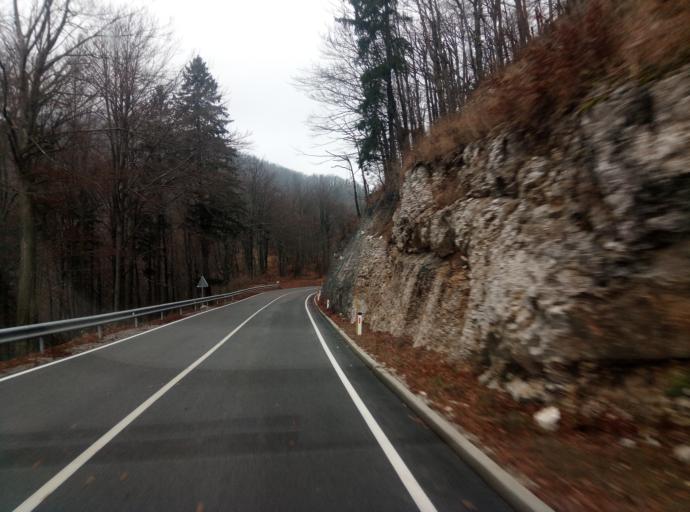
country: SI
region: Idrija
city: Idrija
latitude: 45.9211
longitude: 14.0345
